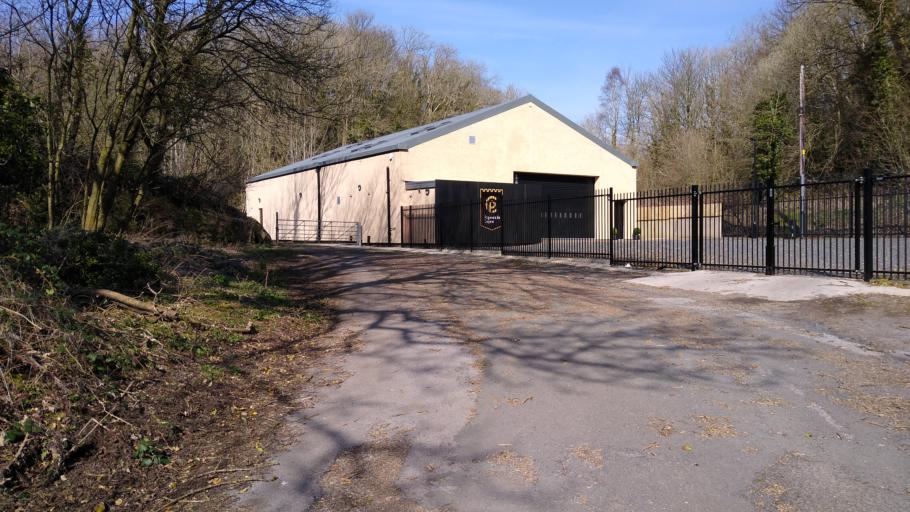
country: GB
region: England
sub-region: Cumbria
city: Dearham
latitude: 54.6718
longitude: -3.4116
